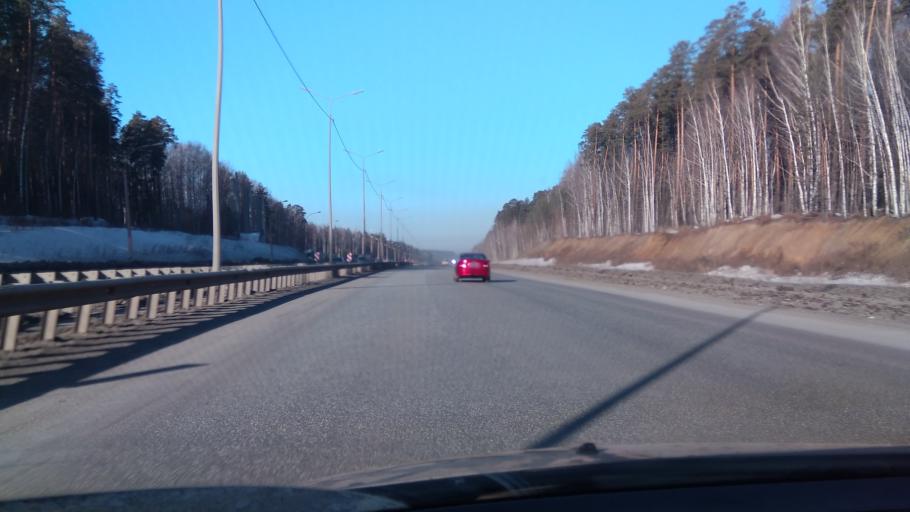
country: RU
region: Sverdlovsk
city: Shirokaya Rechka
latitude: 56.8259
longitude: 60.4507
